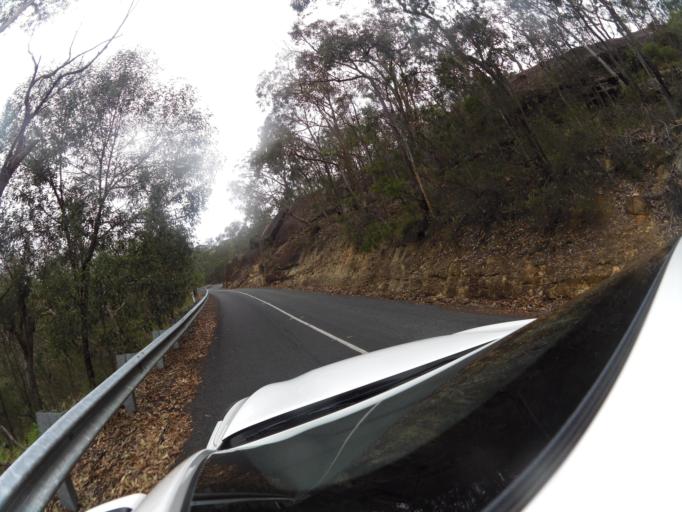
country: AU
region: New South Wales
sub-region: Hawkesbury
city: Pitt Town
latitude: -33.4350
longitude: 150.9259
